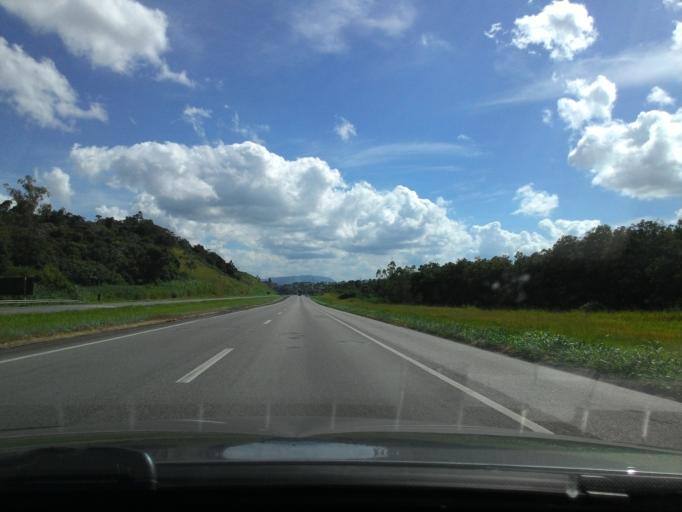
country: BR
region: Sao Paulo
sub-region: Cajati
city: Cajati
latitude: -24.7239
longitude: -48.0866
